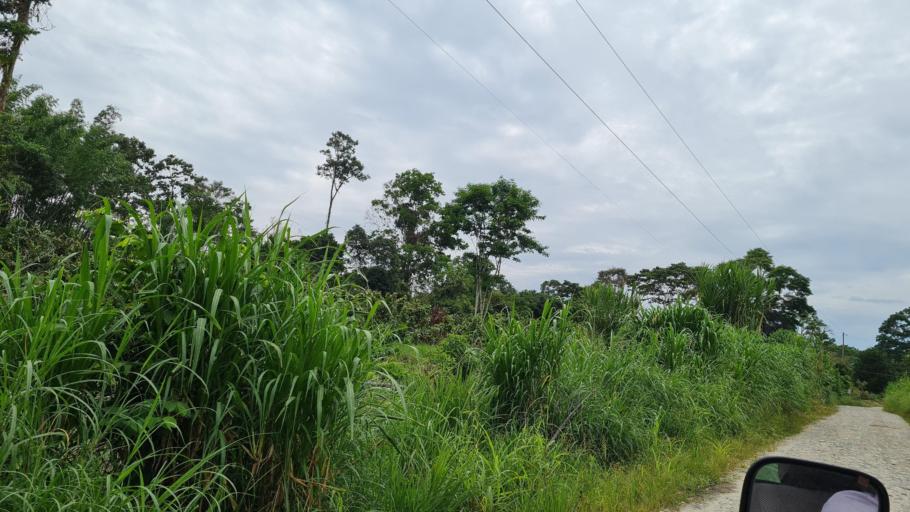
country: EC
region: Napo
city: Tena
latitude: -1.0028
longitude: -77.7685
